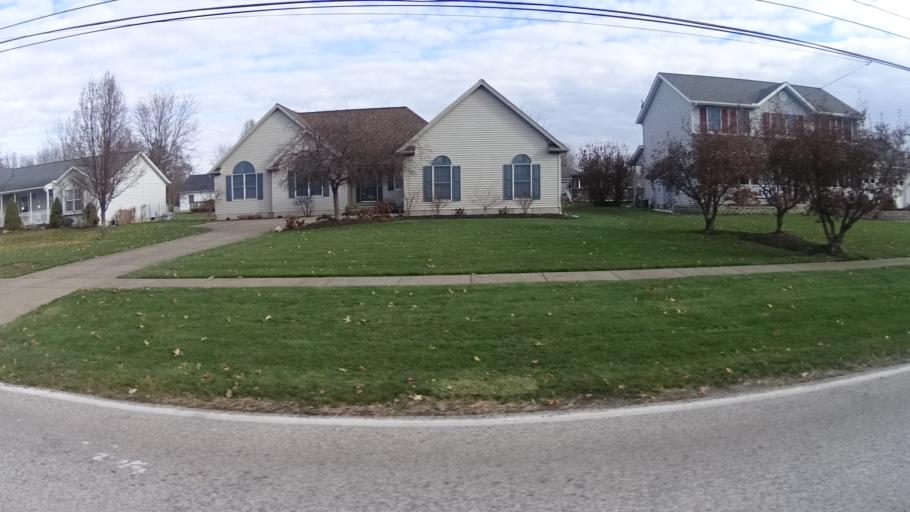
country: US
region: Ohio
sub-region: Lorain County
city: North Ridgeville
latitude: 41.3591
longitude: -81.9914
